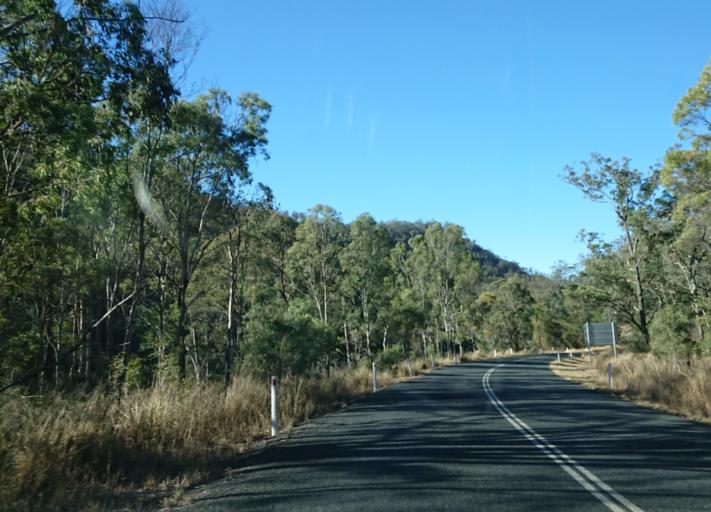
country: AU
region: Queensland
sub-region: Toowoomba
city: Top Camp
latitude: -27.7511
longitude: 152.0829
